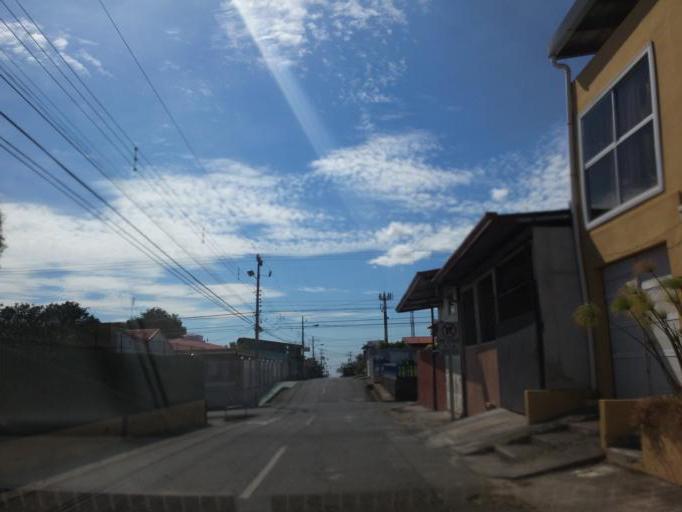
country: CR
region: Heredia
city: Santo Domingo
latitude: 10.0388
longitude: -84.1582
